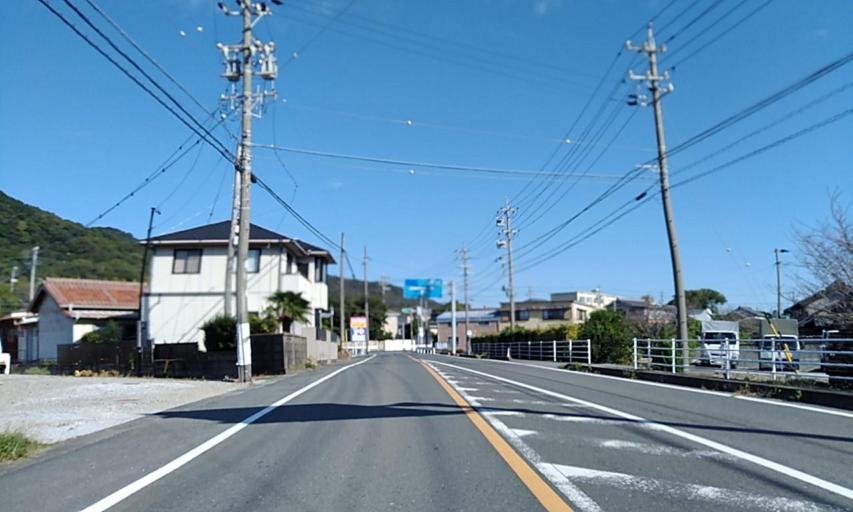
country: JP
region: Aichi
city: Tahara
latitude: 34.6543
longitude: 137.2434
